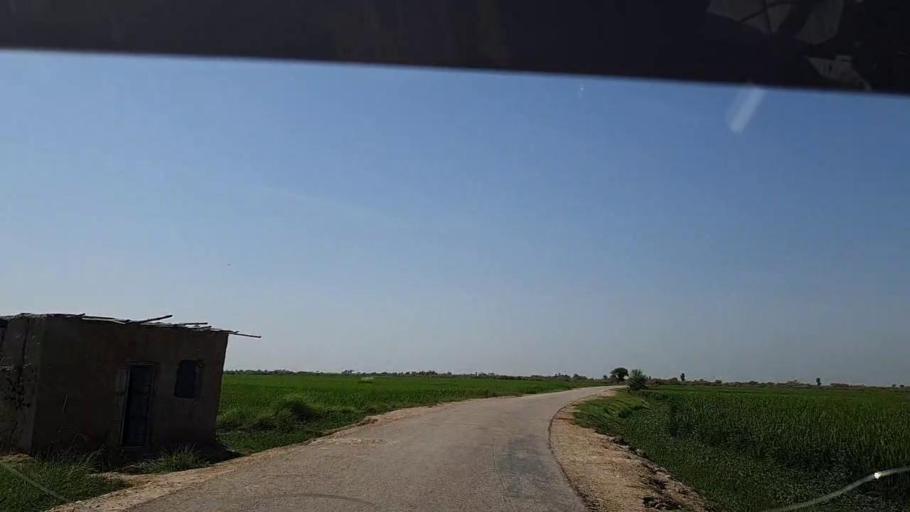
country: PK
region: Sindh
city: Kandhkot
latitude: 28.3110
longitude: 69.1023
